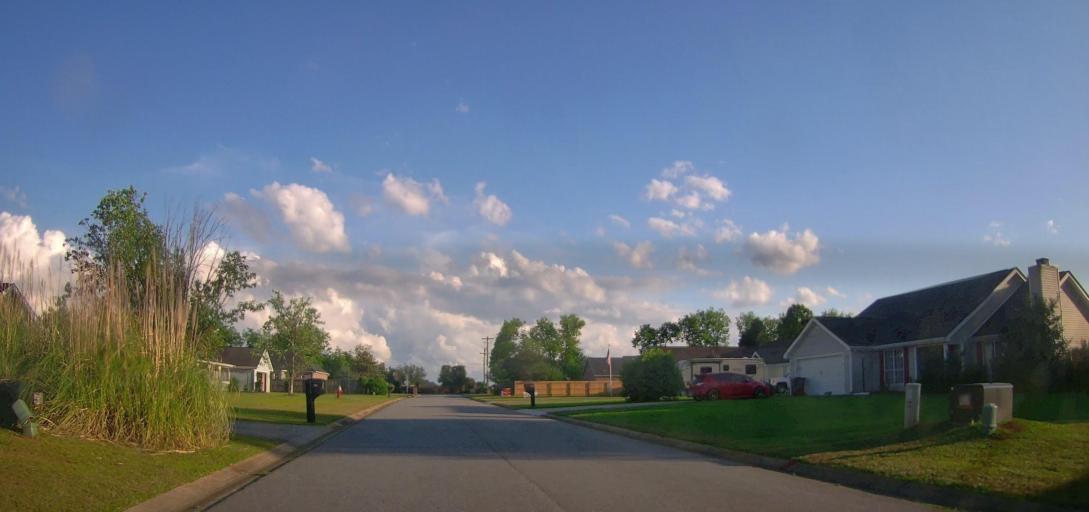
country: US
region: Georgia
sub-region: Houston County
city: Centerville
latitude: 32.6362
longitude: -83.7206
